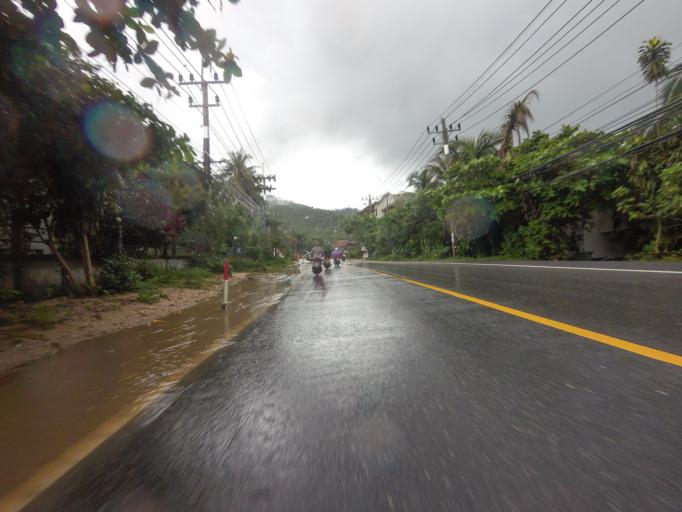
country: TH
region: Surat Thani
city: Ko Samui
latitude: 9.4482
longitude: 100.0269
